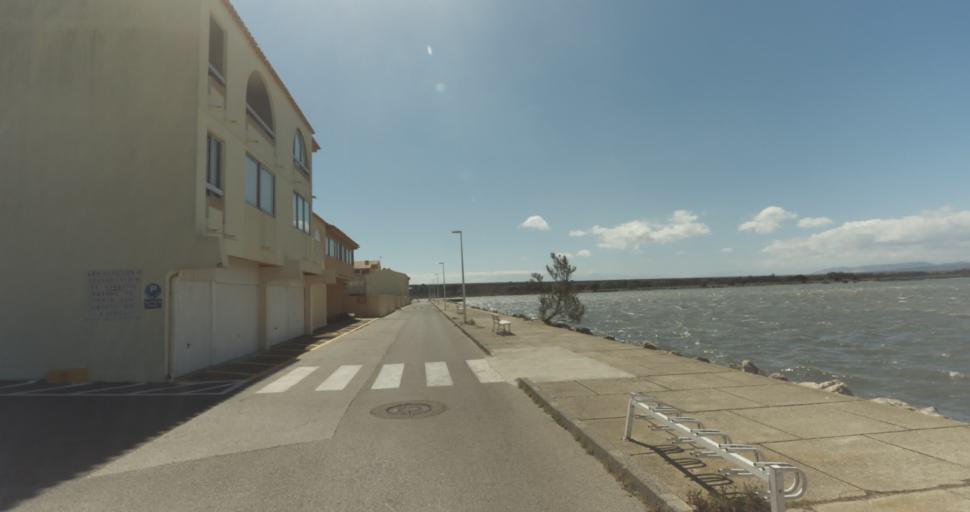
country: FR
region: Languedoc-Roussillon
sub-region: Departement de l'Aude
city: Leucate
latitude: 42.8613
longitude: 3.0360
